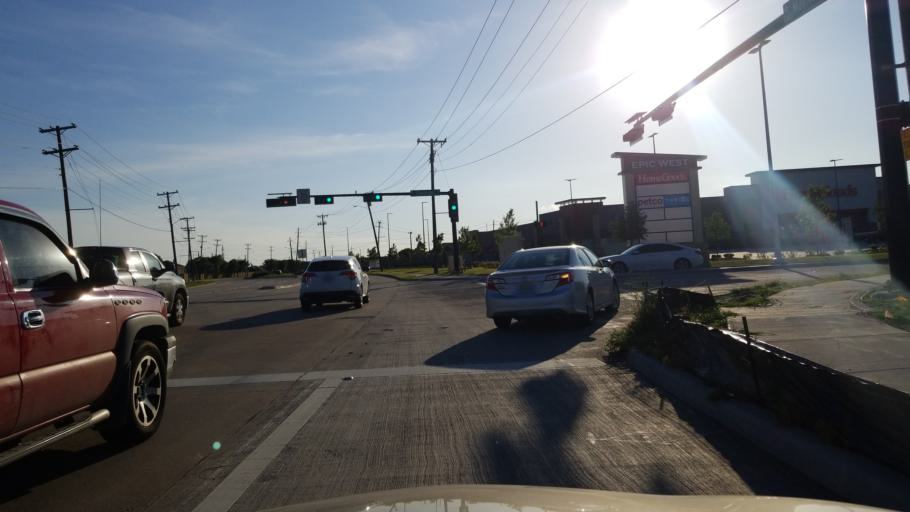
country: US
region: Texas
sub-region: Dallas County
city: Grand Prairie
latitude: 32.6919
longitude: -97.0265
